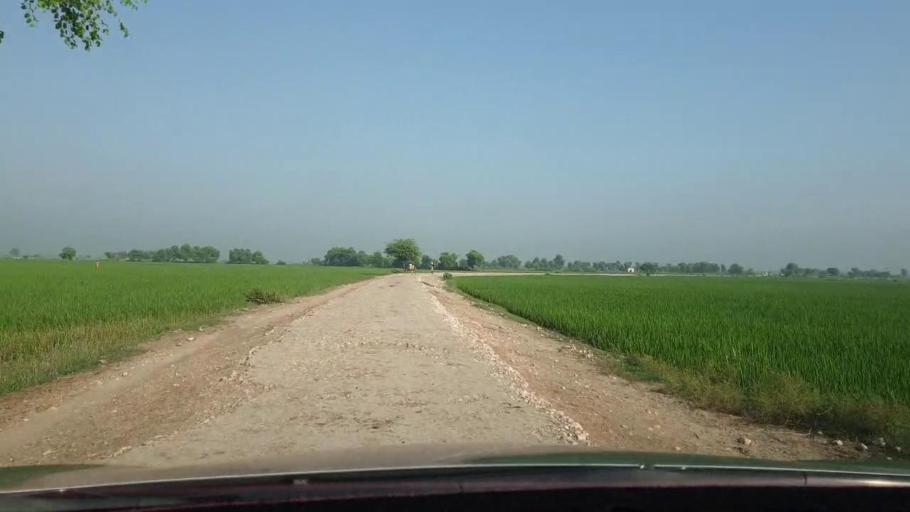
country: PK
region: Sindh
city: Nasirabad
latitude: 27.4292
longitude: 67.9211
